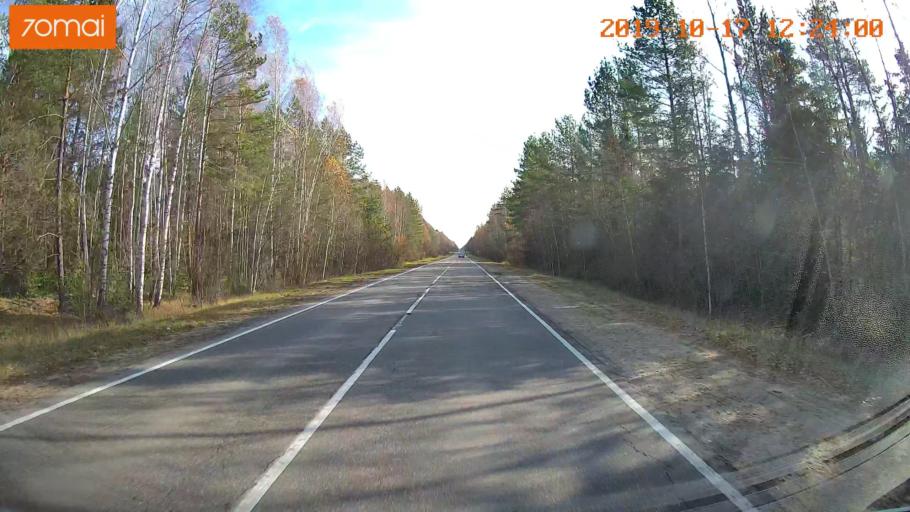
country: RU
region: Rjazan
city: Gus'-Zheleznyy
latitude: 55.0391
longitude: 41.2057
